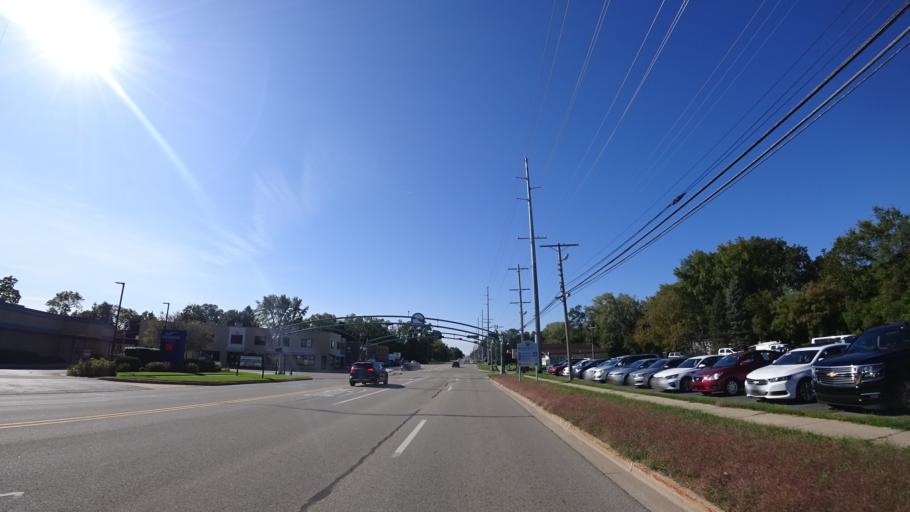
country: US
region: Michigan
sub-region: Berrien County
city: Bridgman
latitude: 41.9436
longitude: -86.5631
